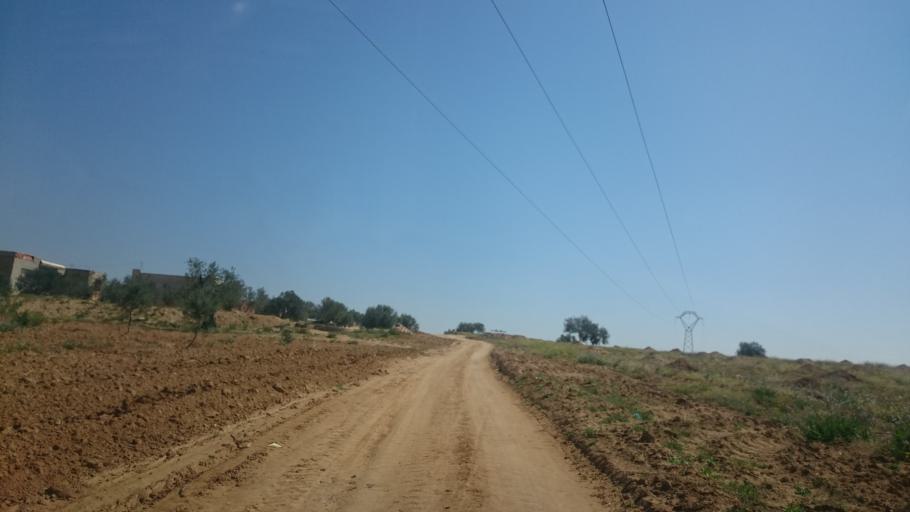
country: TN
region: Safaqis
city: Sfax
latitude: 34.7898
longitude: 10.5427
